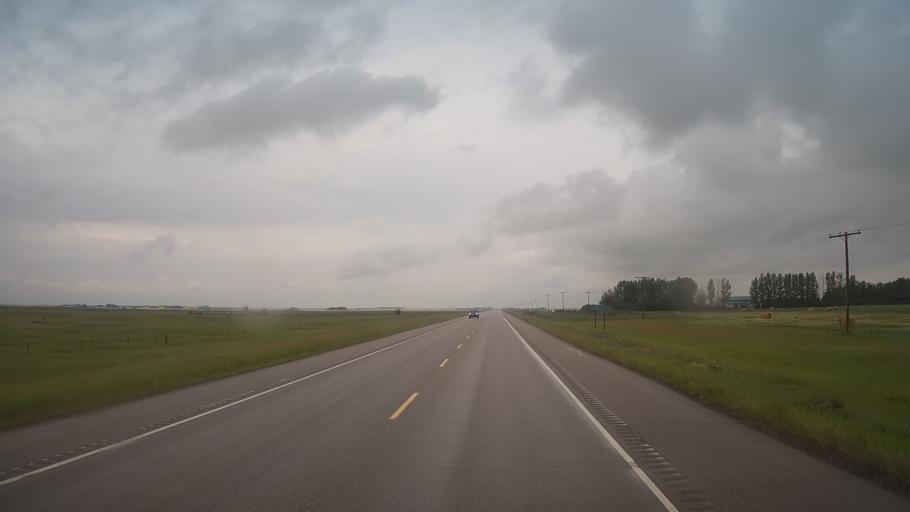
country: CA
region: Saskatchewan
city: Unity
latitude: 52.4349
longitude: -108.9721
